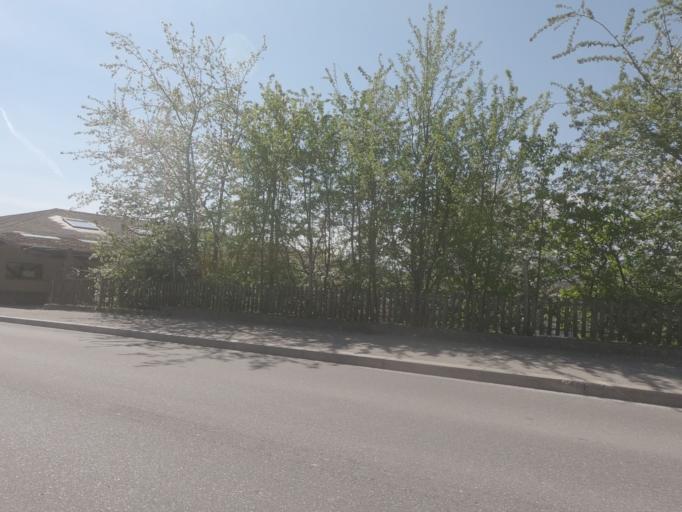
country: CH
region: Bern
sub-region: Biel/Bienne District
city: Meinisberg
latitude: 47.1225
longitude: 7.3422
